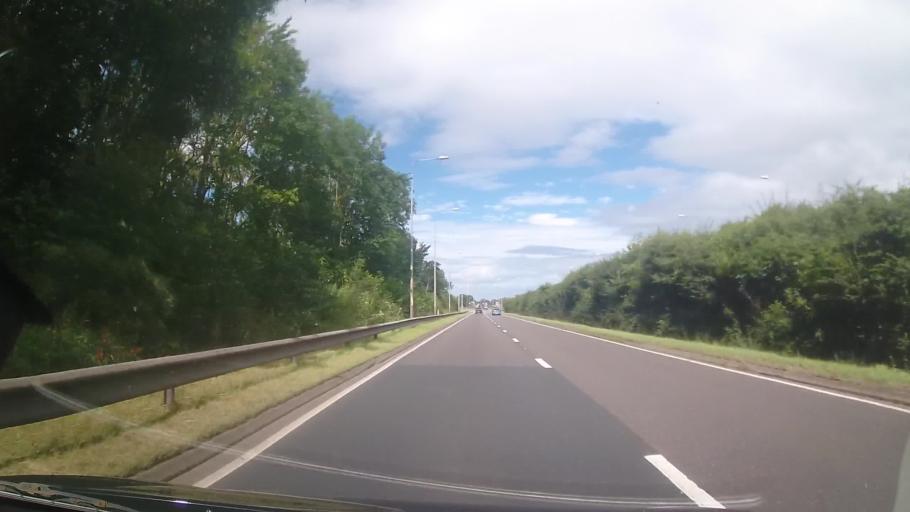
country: GB
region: Wales
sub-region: Denbighshire
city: Bodelwyddan
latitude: 53.2621
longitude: -3.4775
